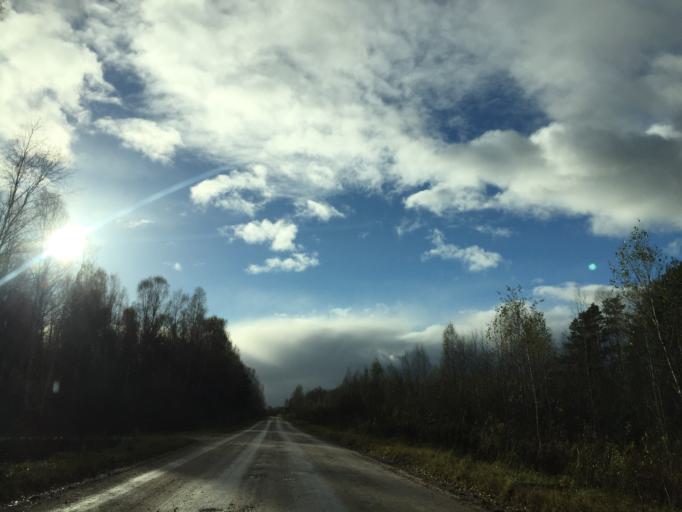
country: LV
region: Tukuma Rajons
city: Tukums
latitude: 56.9762
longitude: 22.9713
